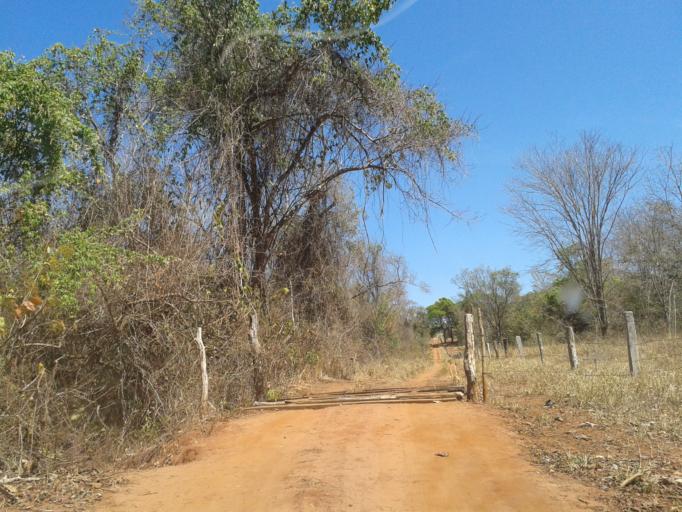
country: BR
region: Minas Gerais
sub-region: Ituiutaba
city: Ituiutaba
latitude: -19.1248
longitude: -49.3010
